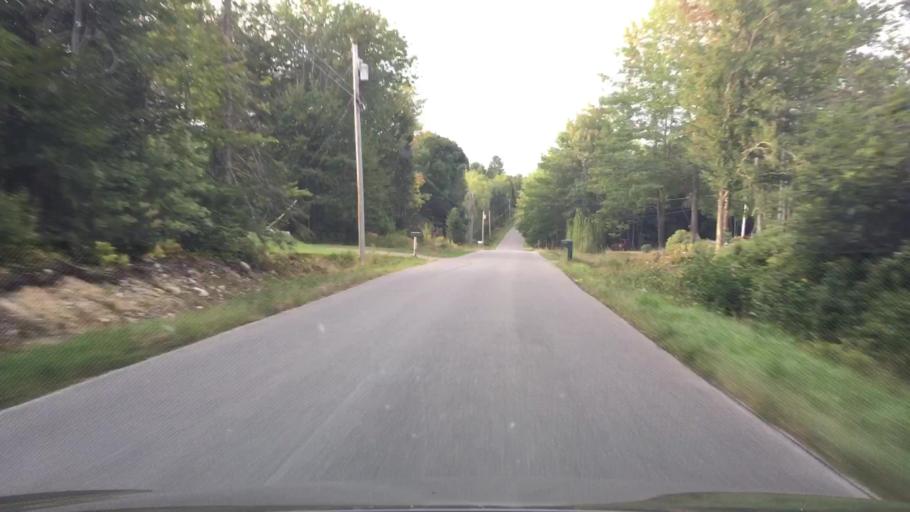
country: US
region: Maine
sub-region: Waldo County
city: Stockton Springs
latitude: 44.4989
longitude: -68.8746
